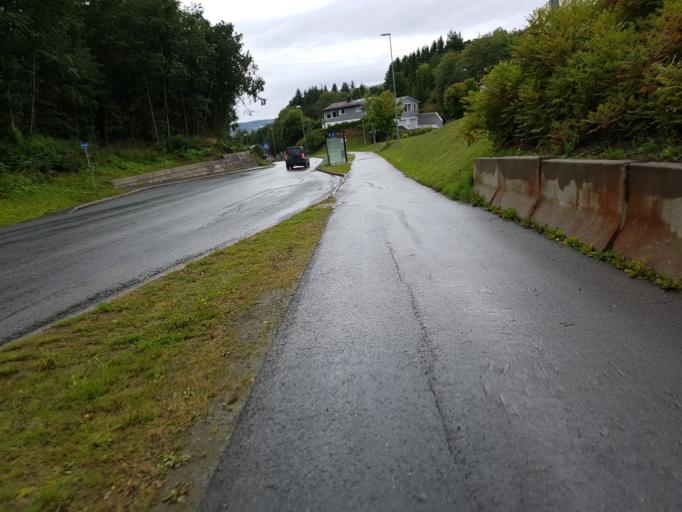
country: NO
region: Sor-Trondelag
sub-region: Trondheim
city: Trondheim
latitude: 63.3851
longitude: 10.4277
